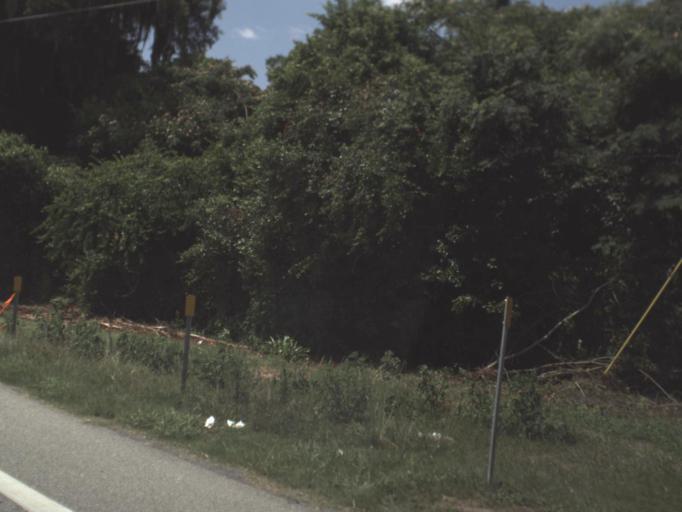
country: US
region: Florida
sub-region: Madison County
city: Madison
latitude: 30.4759
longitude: -83.6347
